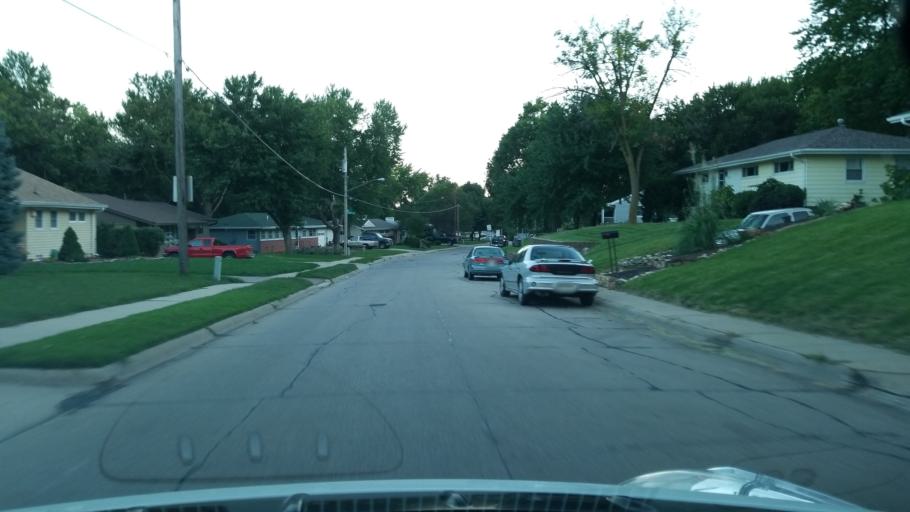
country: US
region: Nebraska
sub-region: Sarpy County
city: Bellevue
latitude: 41.1438
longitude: -95.9013
